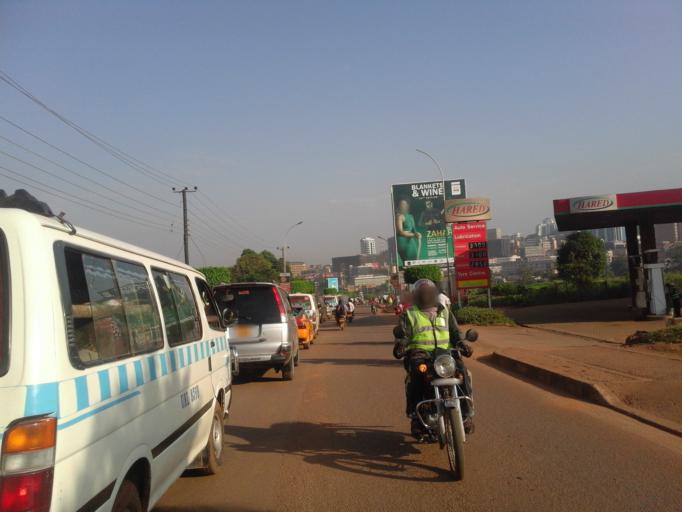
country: UG
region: Central Region
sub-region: Kampala District
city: Kampala
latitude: 0.3045
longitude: 32.5845
